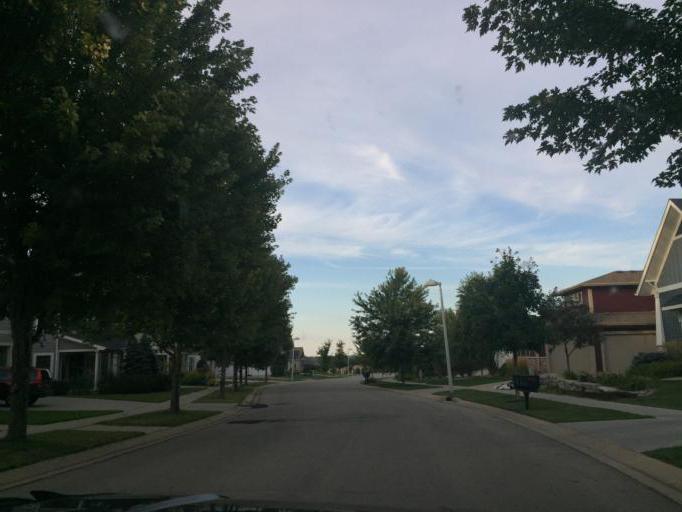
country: US
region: Minnesota
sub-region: Olmsted County
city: Rochester
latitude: 44.0116
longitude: -92.5015
